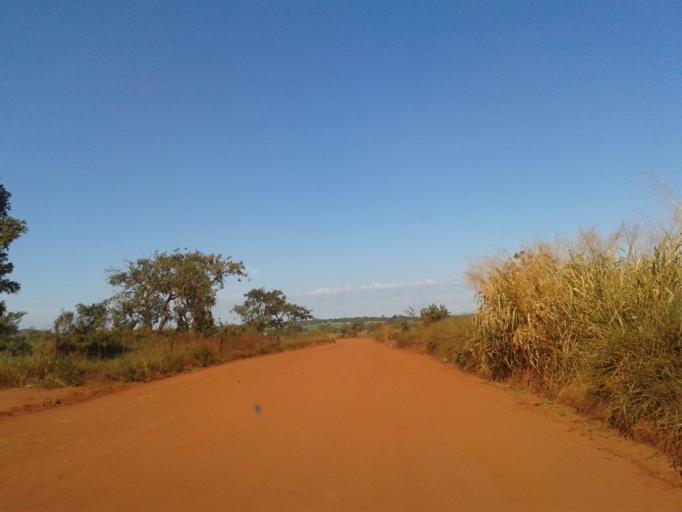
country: BR
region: Minas Gerais
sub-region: Ituiutaba
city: Ituiutaba
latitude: -18.9998
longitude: -49.4905
